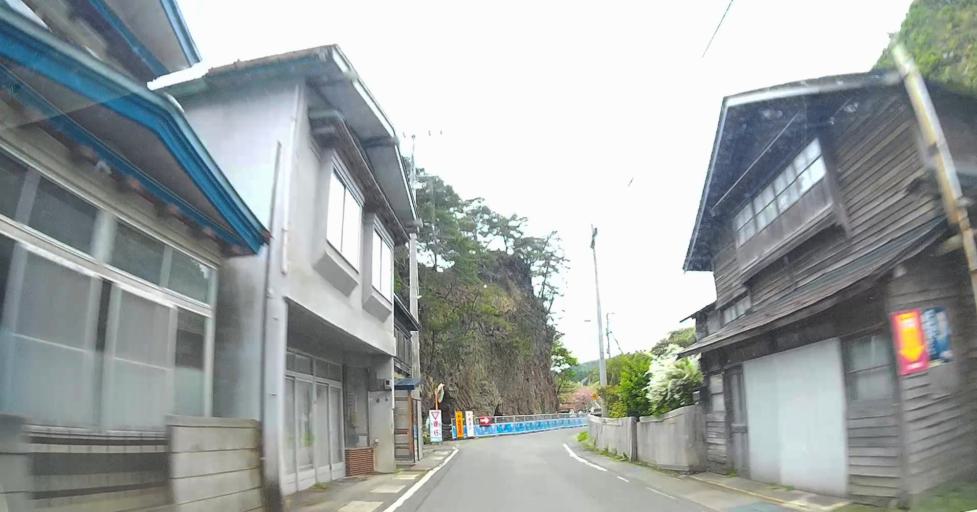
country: JP
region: Aomori
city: Shimokizukuri
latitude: 41.1996
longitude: 140.4300
